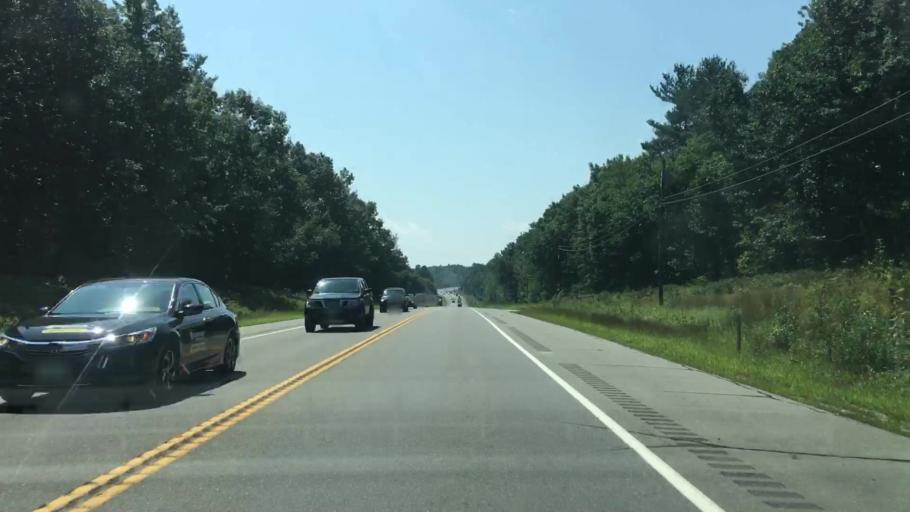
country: US
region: New Hampshire
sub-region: Rockingham County
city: Hampstead
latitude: 42.8442
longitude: -71.2251
